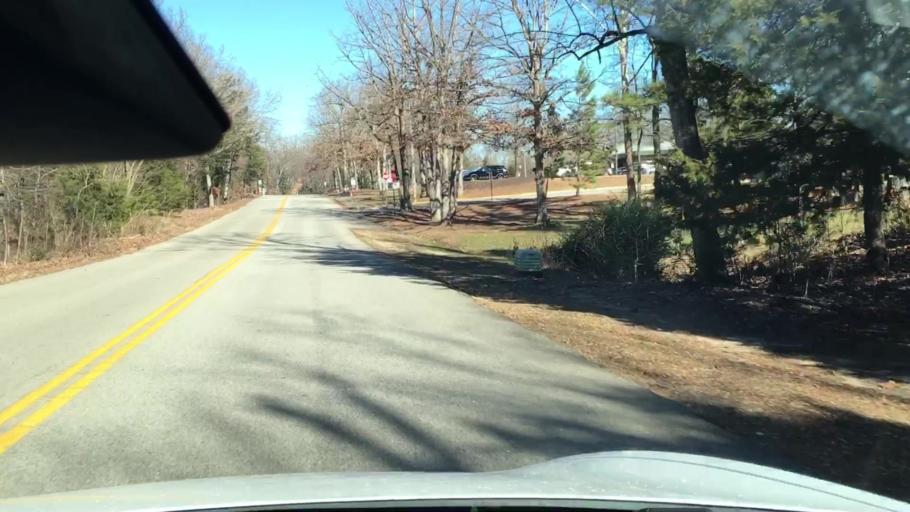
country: US
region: Virginia
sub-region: Chesterfield County
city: Bon Air
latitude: 37.5302
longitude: -77.6148
